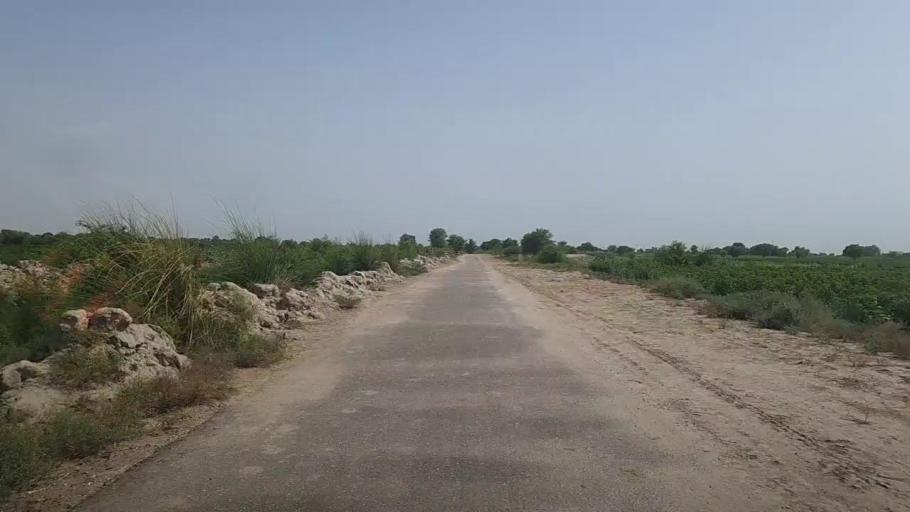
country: PK
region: Sindh
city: Pad Idan
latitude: 26.8323
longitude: 68.3306
